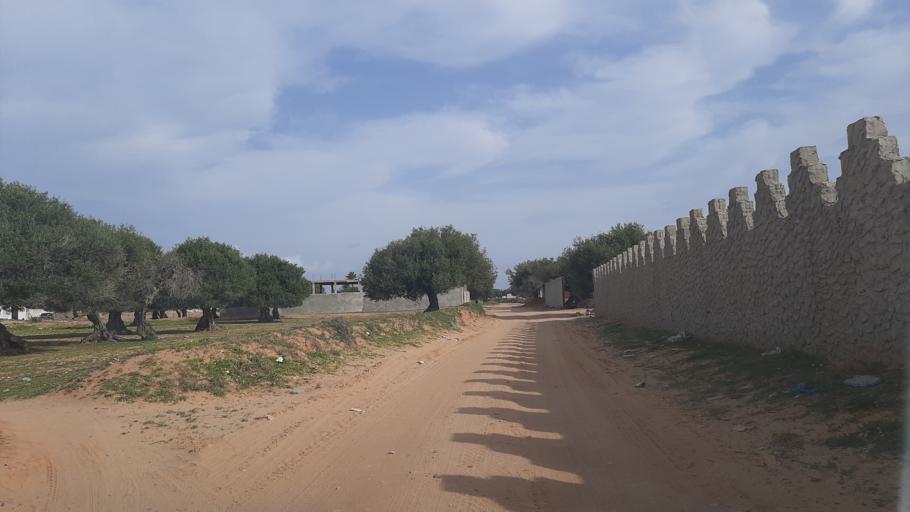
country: TN
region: Madanin
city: Midoun
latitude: 33.8081
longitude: 11.0237
